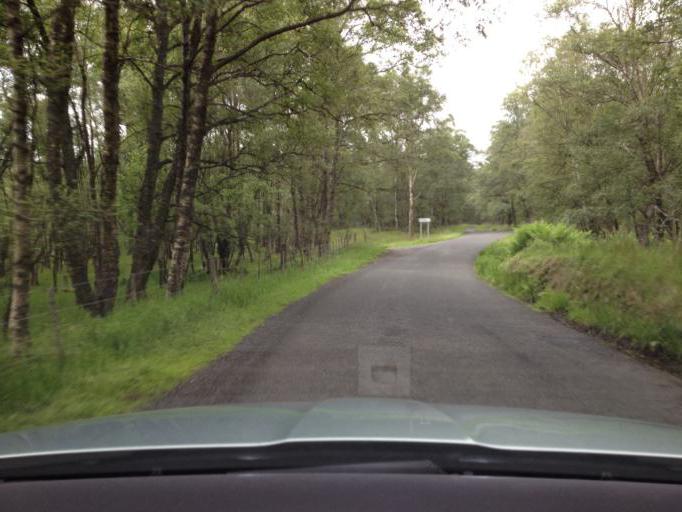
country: GB
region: Scotland
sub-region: Aberdeenshire
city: Aboyne
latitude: 56.8966
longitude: -2.8682
